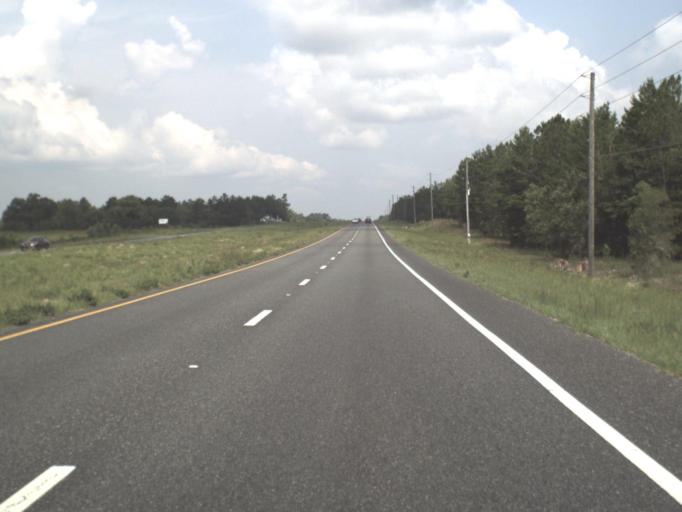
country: US
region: Florida
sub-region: Levy County
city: East Bronson
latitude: 29.4151
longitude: -82.5537
